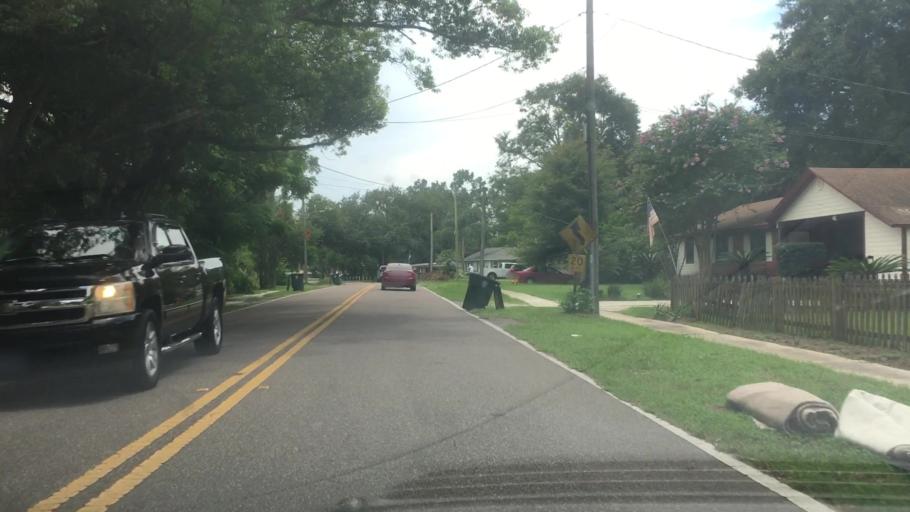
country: US
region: Florida
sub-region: Duval County
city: Jacksonville
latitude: 30.2906
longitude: -81.5484
